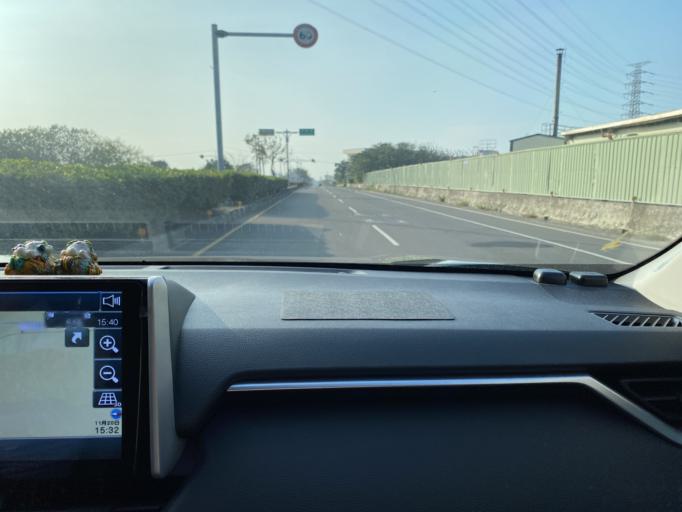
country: TW
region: Taiwan
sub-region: Changhua
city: Chang-hua
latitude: 23.9586
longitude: 120.4024
